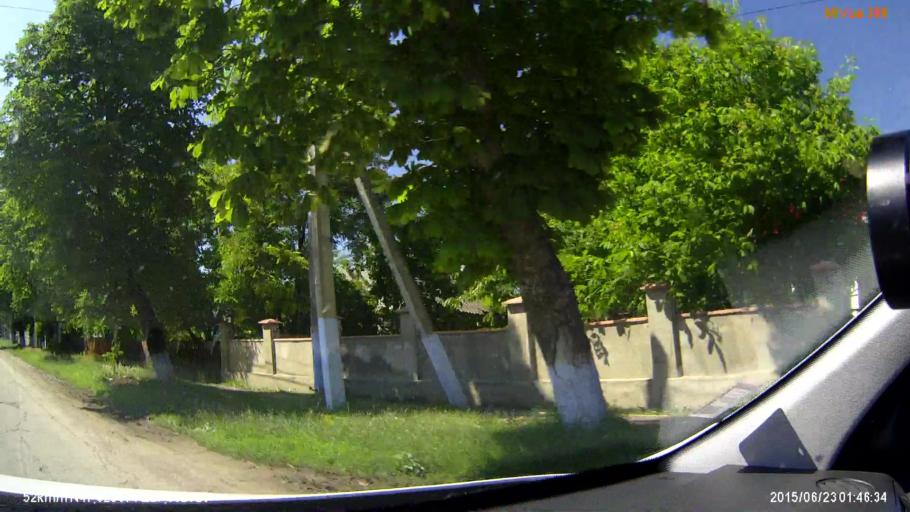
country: RO
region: Iasi
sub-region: Comuna Victoria
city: Victoria
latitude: 47.3256
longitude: 27.6331
